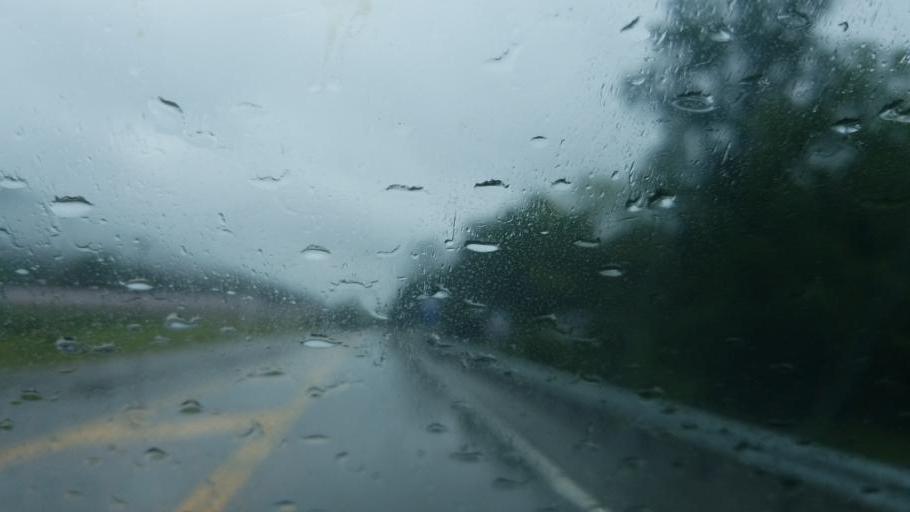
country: US
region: Kentucky
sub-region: Fleming County
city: Flemingsburg
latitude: 38.3349
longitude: -83.5943
